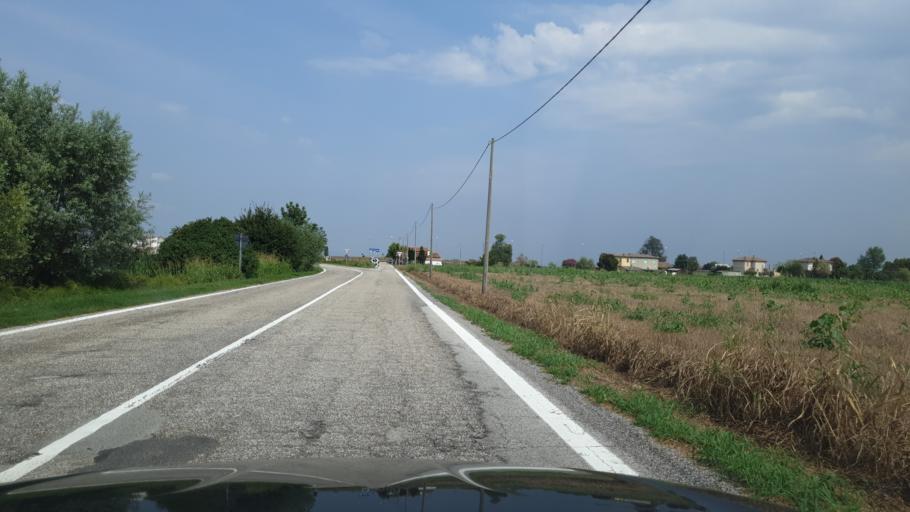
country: IT
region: Veneto
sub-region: Provincia di Rovigo
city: Fratta Polesine
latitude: 45.0225
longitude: 11.6624
